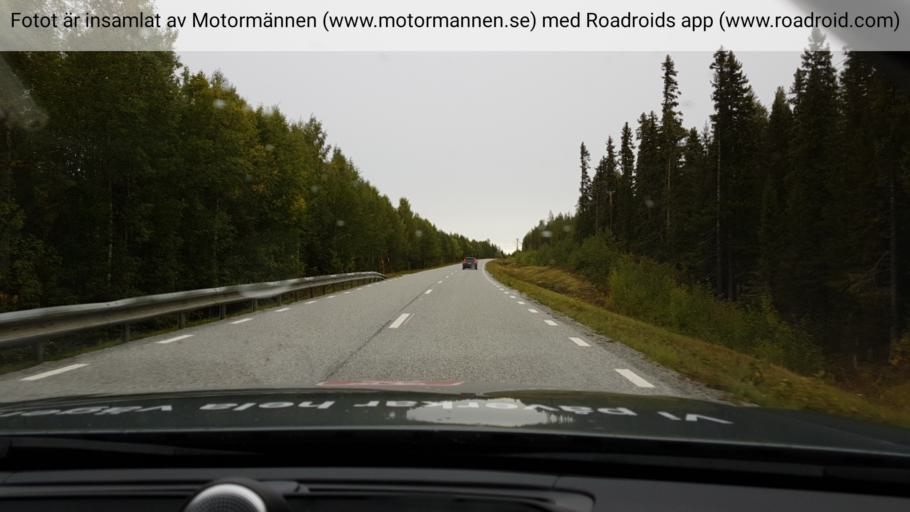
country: SE
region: Jaemtland
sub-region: Stroemsunds Kommun
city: Stroemsund
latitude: 63.9565
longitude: 15.4821
